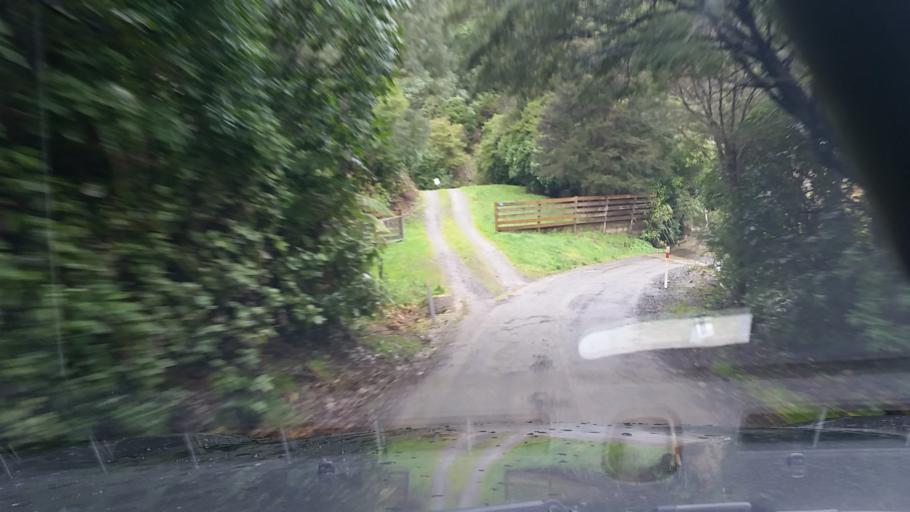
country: NZ
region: Marlborough
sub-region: Marlborough District
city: Picton
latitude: -41.2883
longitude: 174.0388
